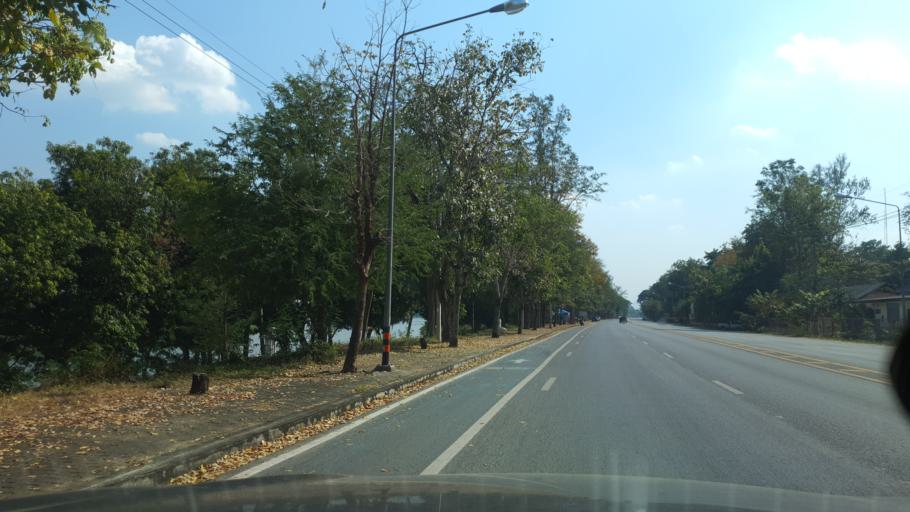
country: TH
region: Tak
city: Tak
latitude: 16.8718
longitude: 99.1183
